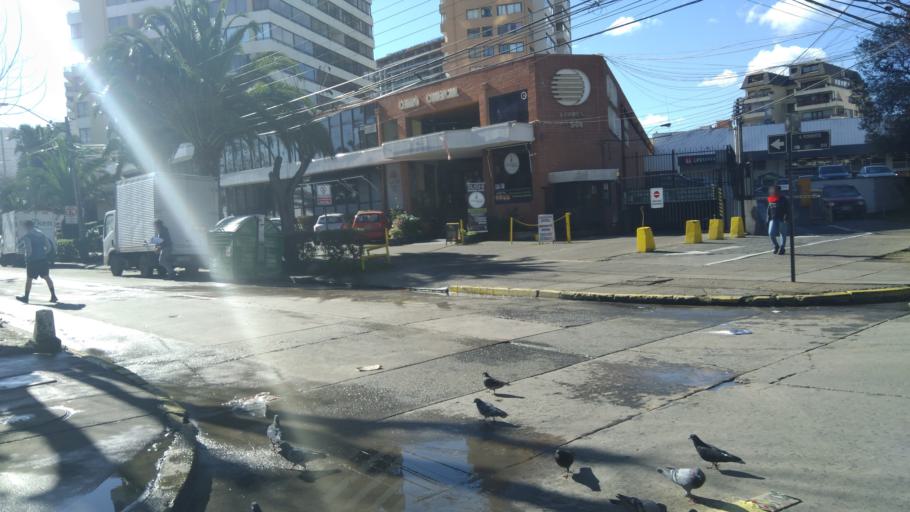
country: CL
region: Valparaiso
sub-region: Provincia de Valparaiso
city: Vina del Mar
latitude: -33.0156
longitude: -71.5552
